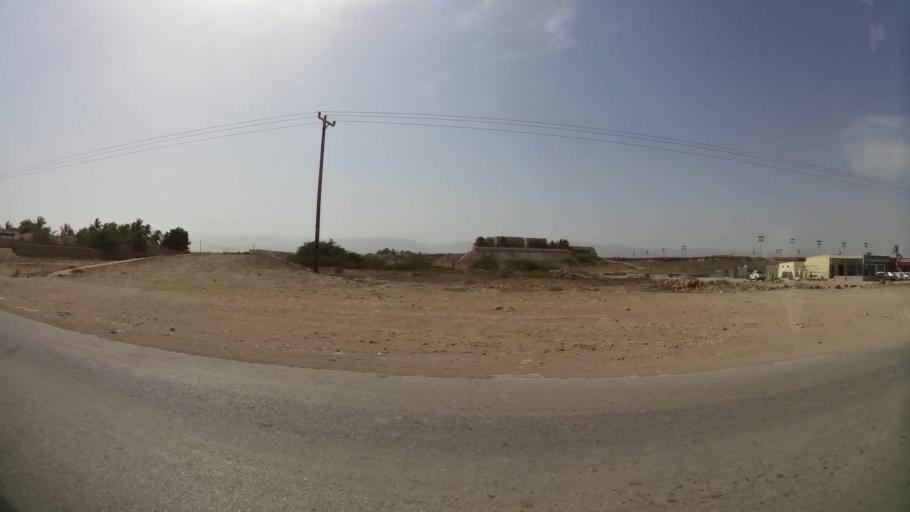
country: OM
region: Zufar
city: Salalah
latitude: 16.9903
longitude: 54.0168
